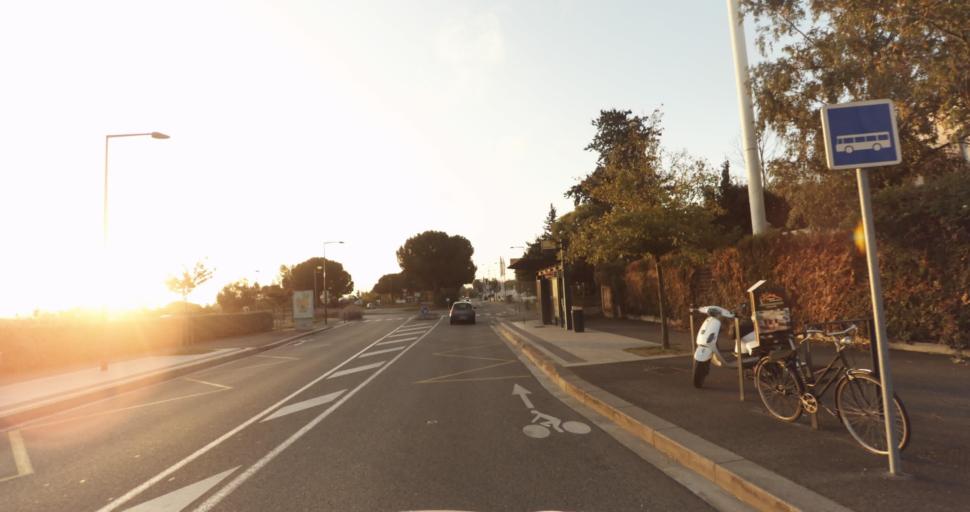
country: FR
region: Midi-Pyrenees
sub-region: Departement de la Haute-Garonne
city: Ramonville-Saint-Agne
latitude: 43.5386
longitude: 1.4806
